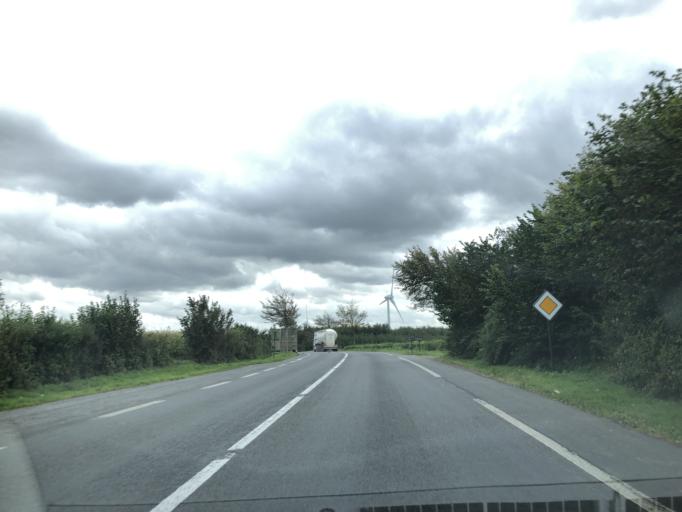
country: FR
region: Nord-Pas-de-Calais
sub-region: Departement du Pas-de-Calais
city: Wailly
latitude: 50.5545
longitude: 2.0986
